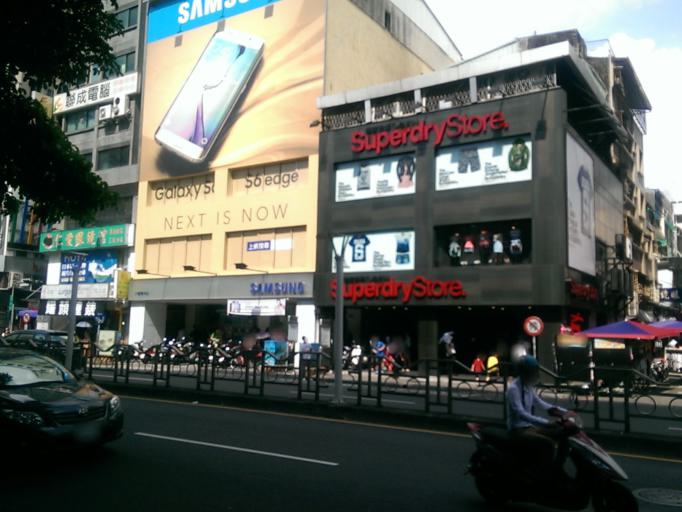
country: TW
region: Taiwan
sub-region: Taichung City
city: Taichung
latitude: 24.1495
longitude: 120.6840
